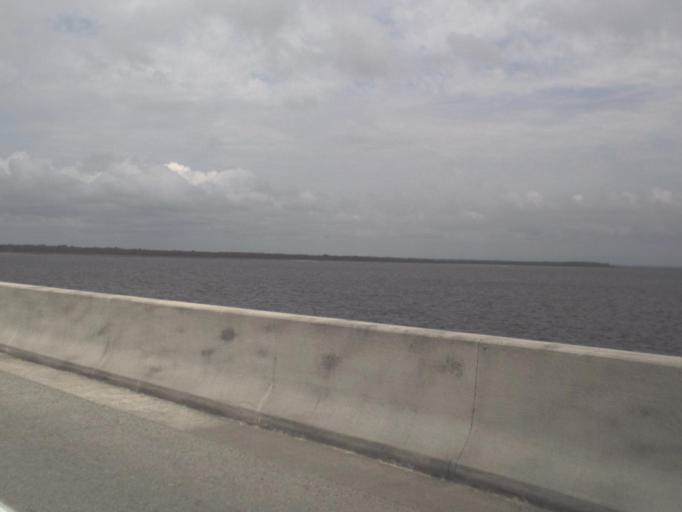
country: US
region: Florida
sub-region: Santa Rosa County
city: Oriole Beach
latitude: 30.4244
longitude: -87.0925
